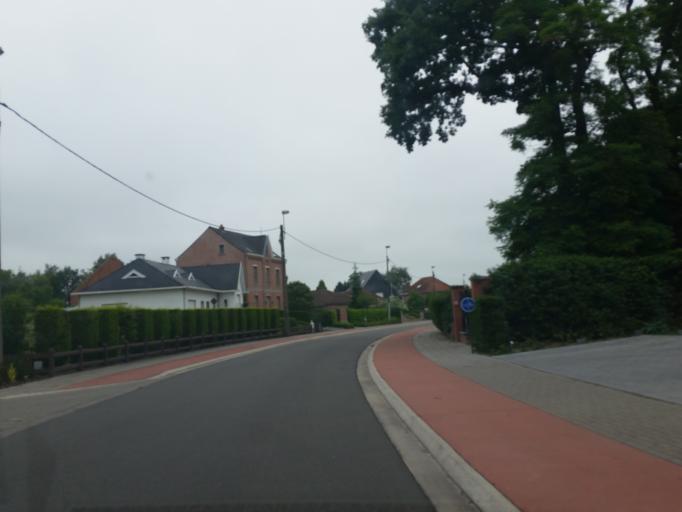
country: BE
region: Flanders
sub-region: Provincie Antwerpen
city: Mechelen
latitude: 50.9940
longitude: 4.4971
